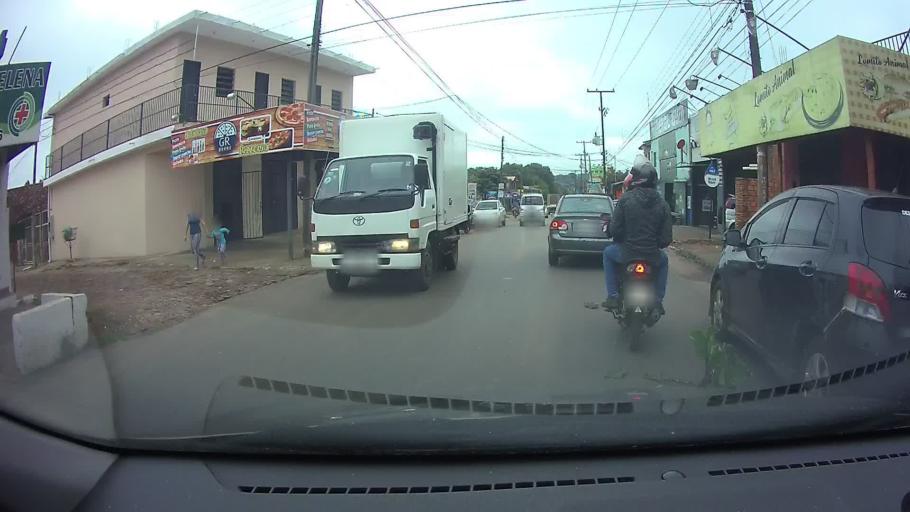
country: PY
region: Central
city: San Lorenzo
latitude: -25.3180
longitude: -57.4952
